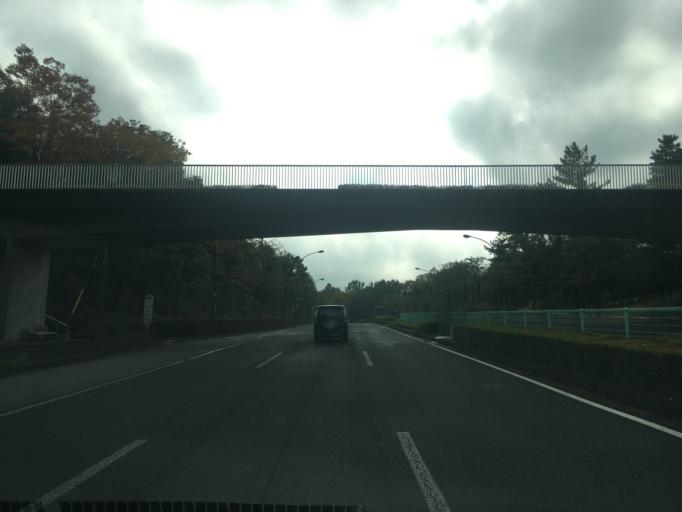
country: JP
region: Tokyo
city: Hino
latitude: 35.6166
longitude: 139.4221
